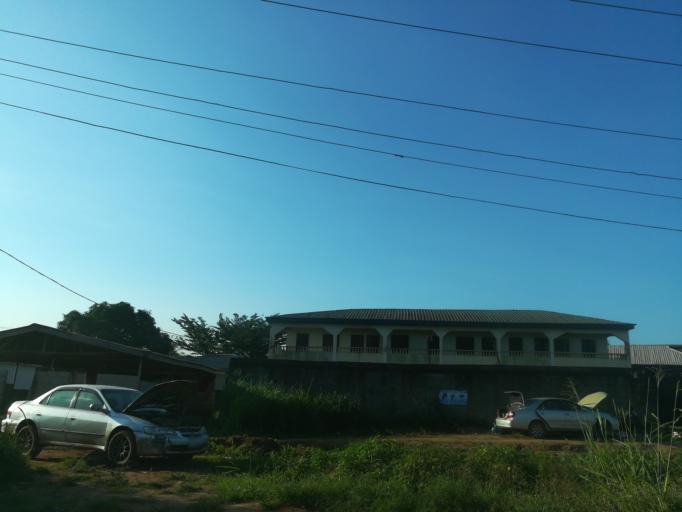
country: NG
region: Lagos
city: Ikorodu
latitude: 6.5916
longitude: 3.5136
